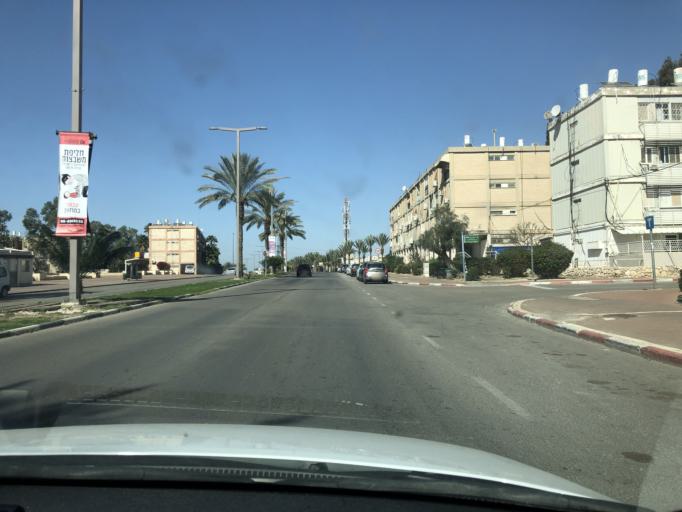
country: IL
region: Southern District
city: Beersheba
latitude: 31.2706
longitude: 34.7981
